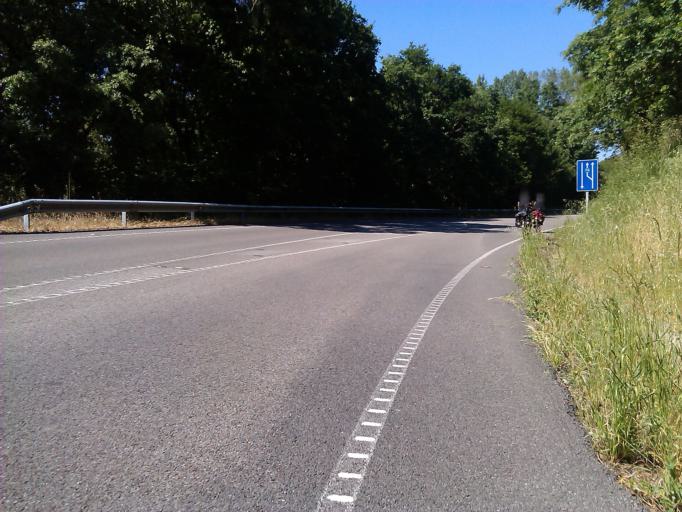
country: ES
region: Galicia
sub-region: Provincia de Lugo
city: Sarria
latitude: 42.7605
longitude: -7.3918
